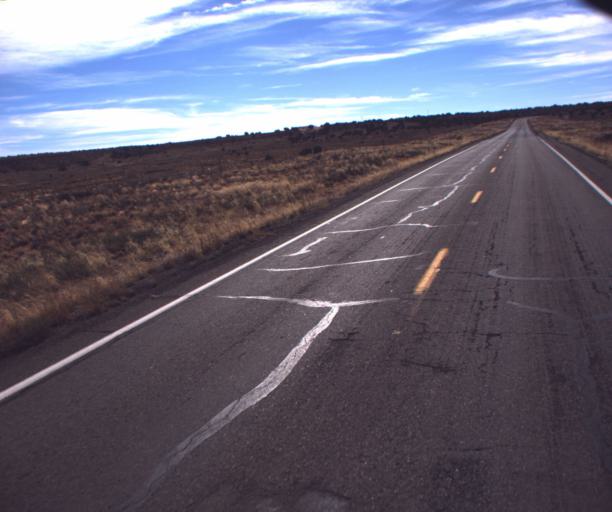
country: US
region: Arizona
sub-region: Coconino County
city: Kaibito
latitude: 36.6875
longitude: -111.2577
